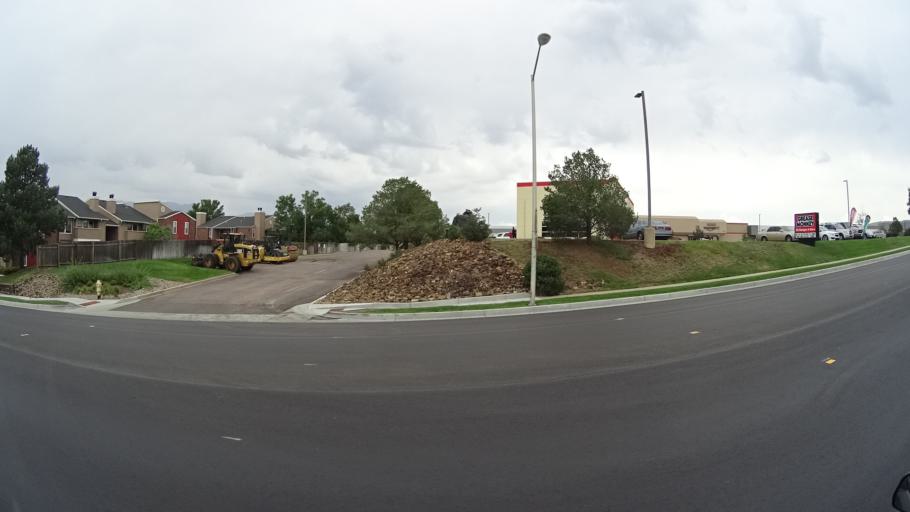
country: US
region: Colorado
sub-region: El Paso County
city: Colorado Springs
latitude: 38.9252
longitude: -104.7960
